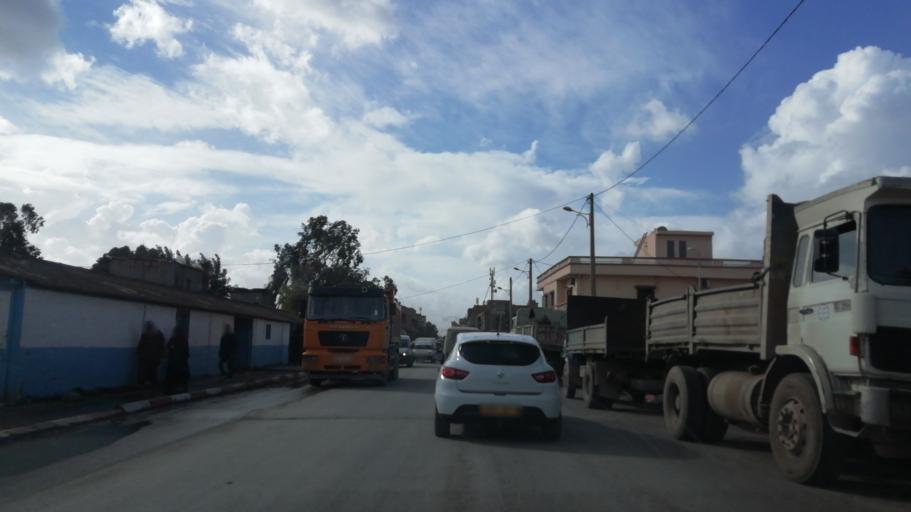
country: DZ
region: Oran
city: Sidi ech Chahmi
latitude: 35.6510
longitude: -0.5686
